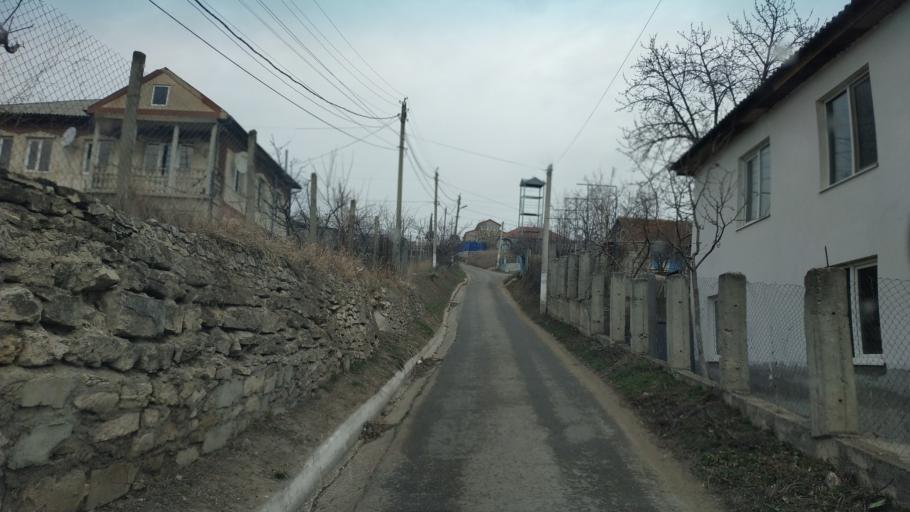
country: MD
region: Chisinau
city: Singera
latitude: 46.9339
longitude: 28.9920
